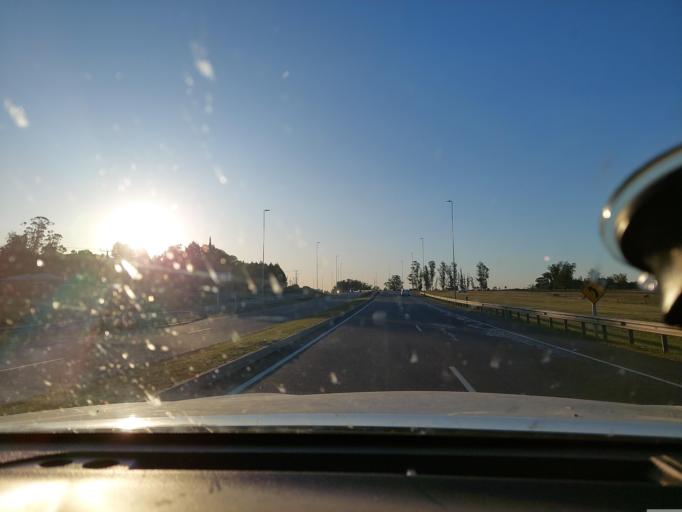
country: UY
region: Canelones
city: Empalme Olmos
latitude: -34.7006
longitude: -55.9133
